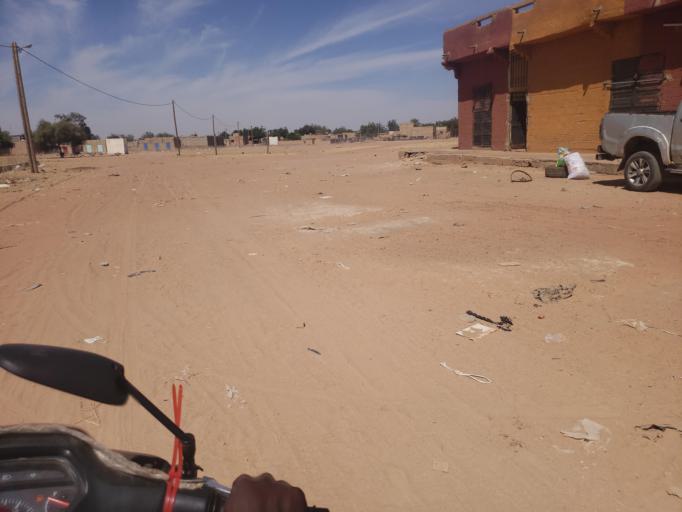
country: SN
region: Matam
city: Ranerou
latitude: 15.2955
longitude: -13.9591
